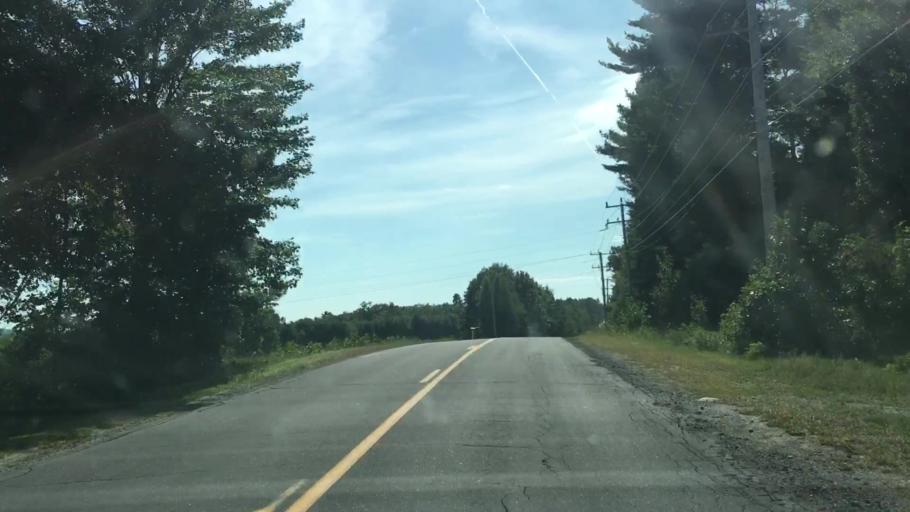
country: US
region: Maine
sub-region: Penobscot County
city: Lincoln
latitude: 45.4337
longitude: -68.4644
